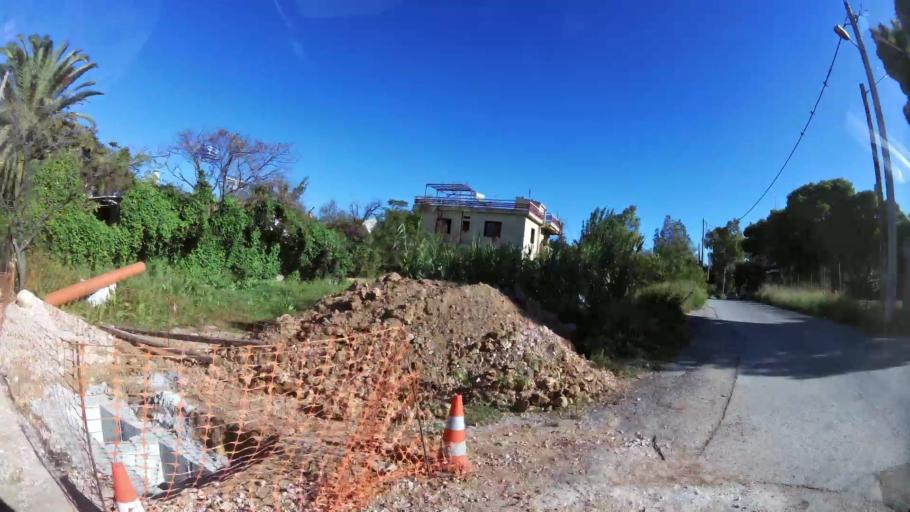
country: GR
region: Attica
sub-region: Nomarchia Athinas
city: Agia Paraskevi
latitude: 38.0211
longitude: 23.8378
